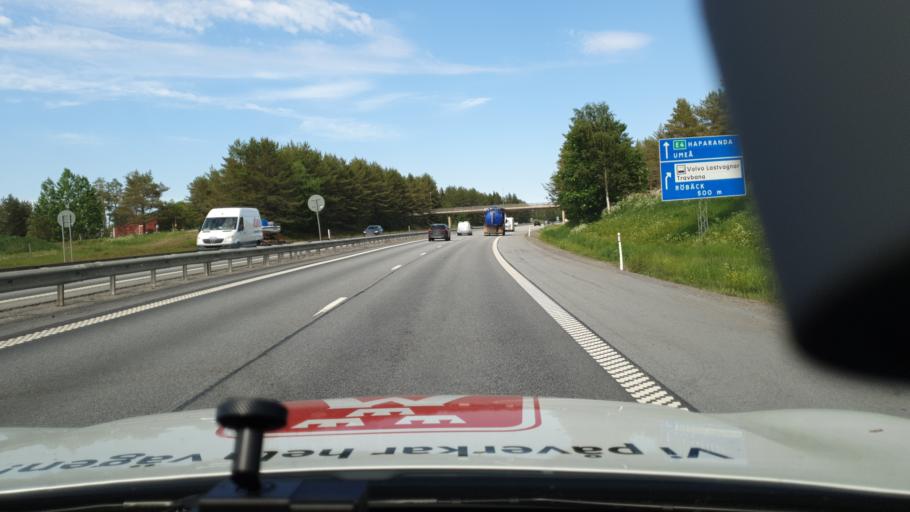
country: SE
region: Vaesterbotten
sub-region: Umea Kommun
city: Roback
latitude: 63.7794
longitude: 20.1916
